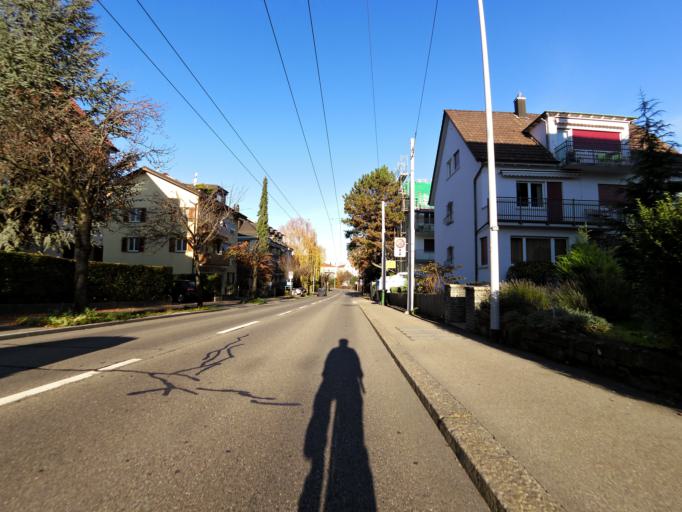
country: CH
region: Zurich
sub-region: Bezirk Zuerich
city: Zuerich (Kreis 3) / Friesenberg
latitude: 47.3652
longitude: 8.5090
